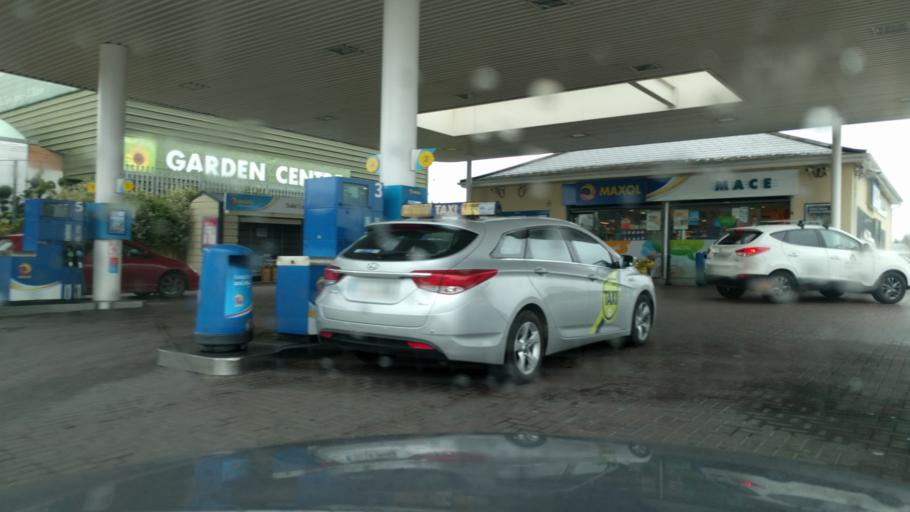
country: IE
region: Leinster
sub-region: Lu
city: Drogheda
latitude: 53.7049
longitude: -6.3748
